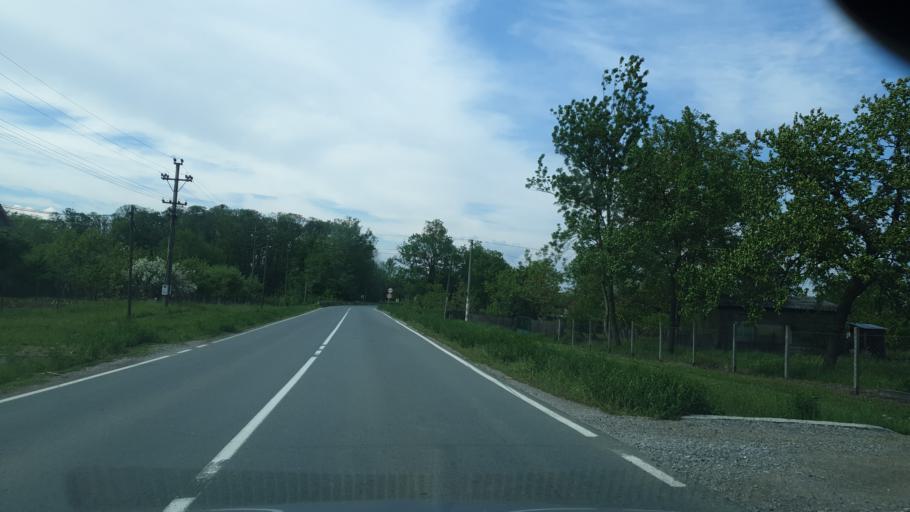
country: RS
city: Stubline
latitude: 44.5937
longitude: 20.1461
